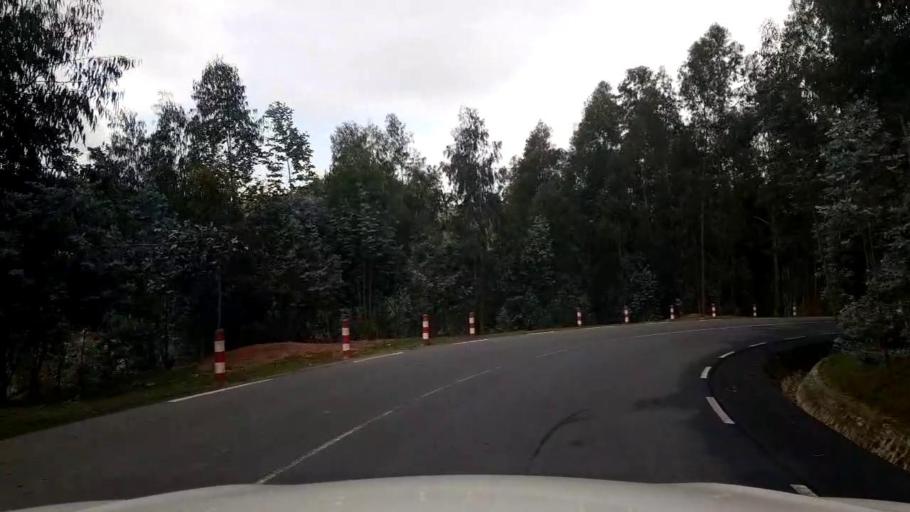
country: RW
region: Northern Province
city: Musanze
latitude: -1.6860
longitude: 29.5226
